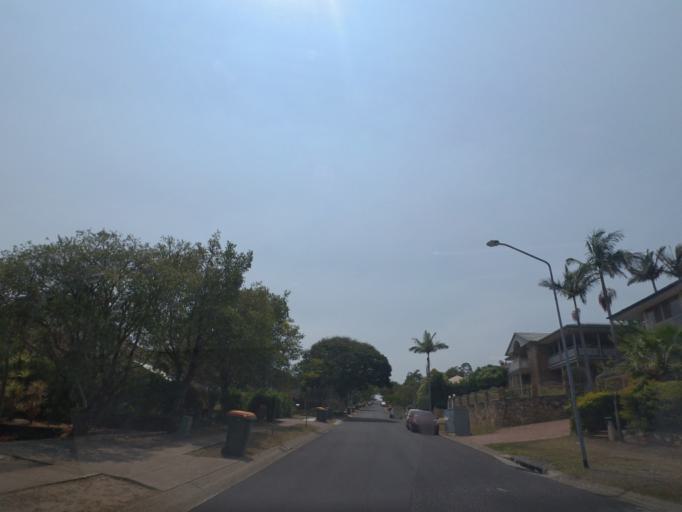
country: AU
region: Queensland
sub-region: Brisbane
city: Nathan
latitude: -27.5608
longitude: 153.0594
